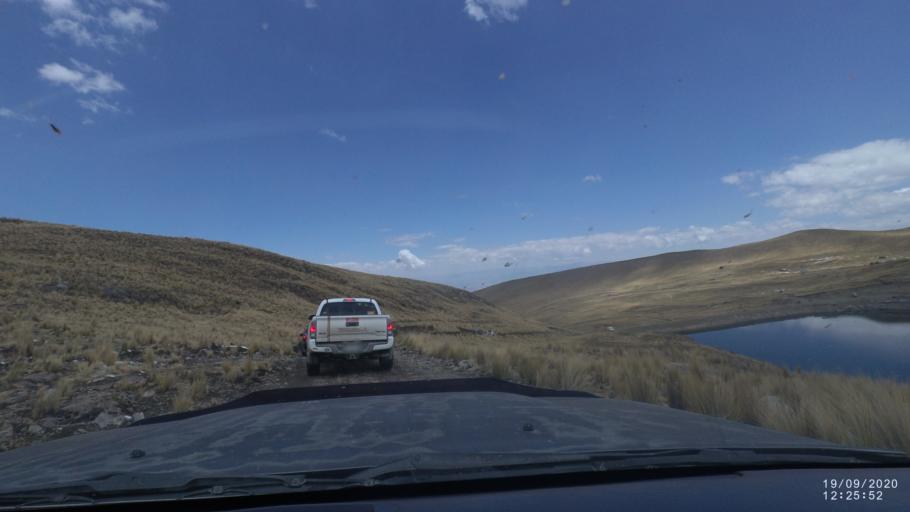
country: BO
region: Cochabamba
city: Cochabamba
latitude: -17.2935
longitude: -66.1113
